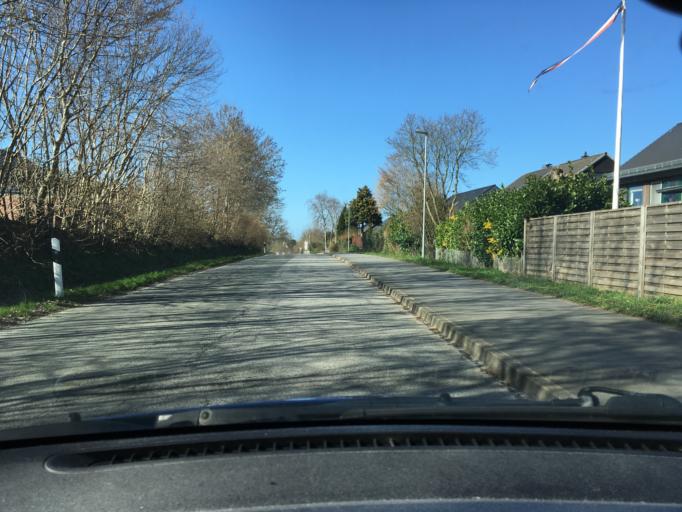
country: DE
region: Schleswig-Holstein
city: Fahrdorf
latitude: 54.5050
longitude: 9.6124
